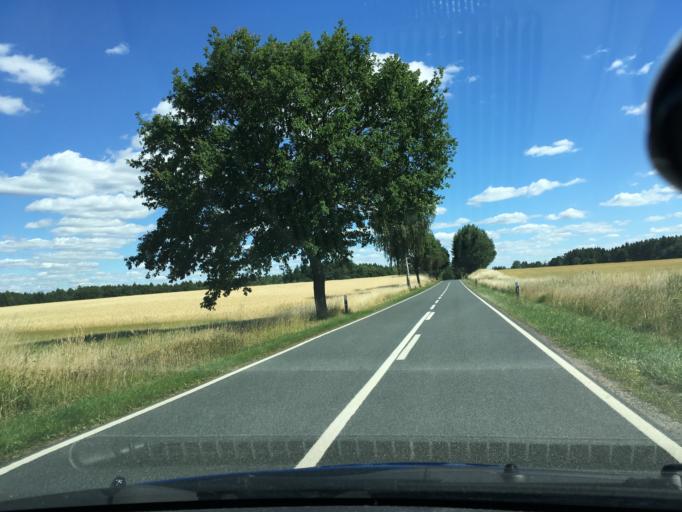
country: DE
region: Lower Saxony
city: Tosterglope
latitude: 53.2126
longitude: 10.8402
